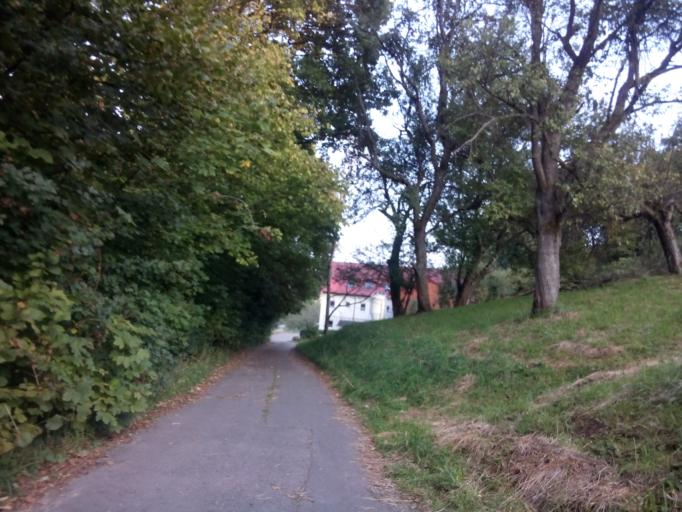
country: DE
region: Baden-Wuerttemberg
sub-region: Tuebingen Region
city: Tuebingen
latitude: 48.5335
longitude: 9.0418
